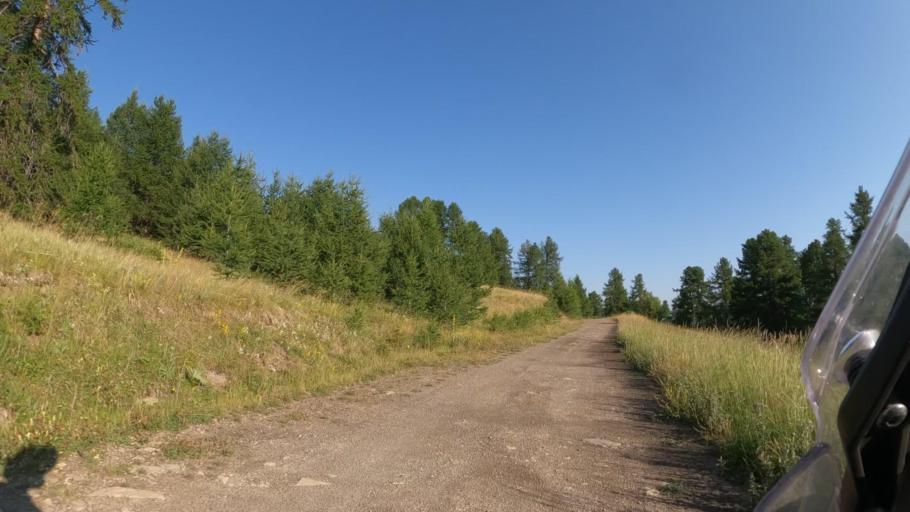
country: FR
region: Provence-Alpes-Cote d'Azur
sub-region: Departement des Hautes-Alpes
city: Guillestre
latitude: 44.6110
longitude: 6.6666
